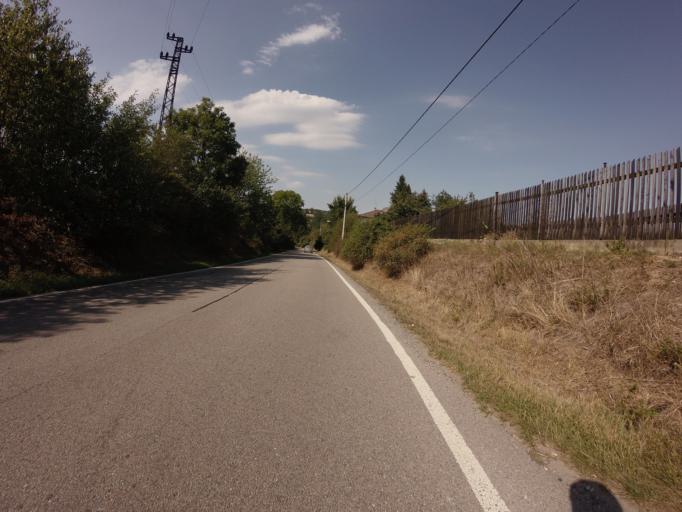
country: CZ
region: Central Bohemia
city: Kamenny Privoz
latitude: 49.8619
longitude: 14.5099
